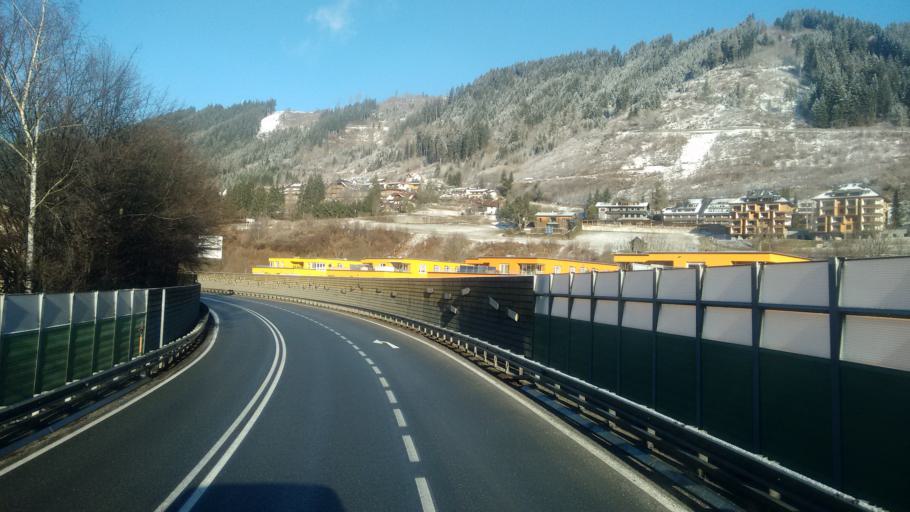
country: AT
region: Styria
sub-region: Politischer Bezirk Liezen
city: Schladming
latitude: 47.3968
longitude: 13.6918
